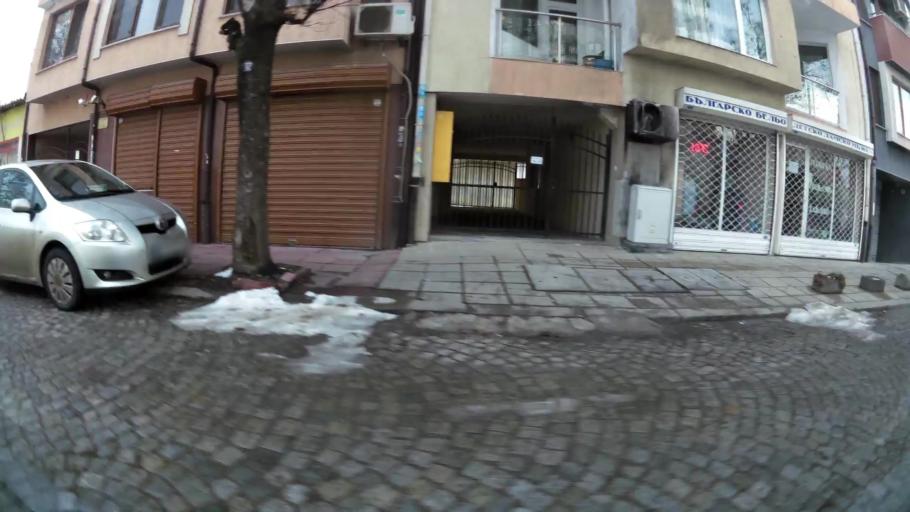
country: BG
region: Sofia-Capital
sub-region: Stolichna Obshtina
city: Sofia
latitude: 42.6954
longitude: 23.2916
